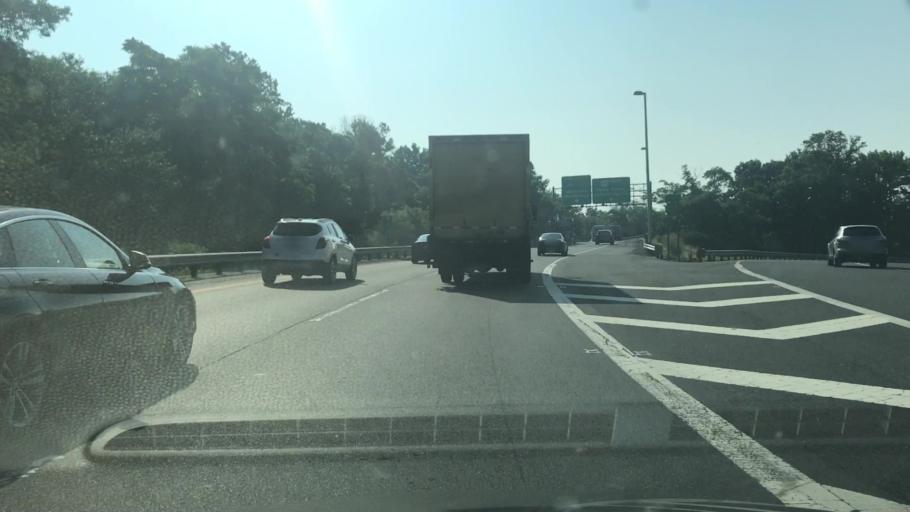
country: US
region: New Jersey
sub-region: Middlesex County
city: Fords
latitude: 40.5261
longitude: -74.3354
